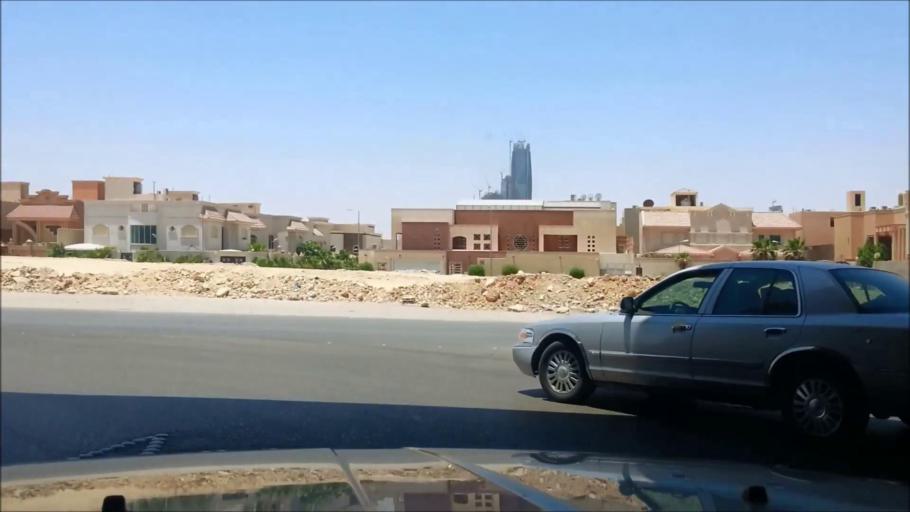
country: SA
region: Ar Riyad
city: Riyadh
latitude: 24.7750
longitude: 46.6657
